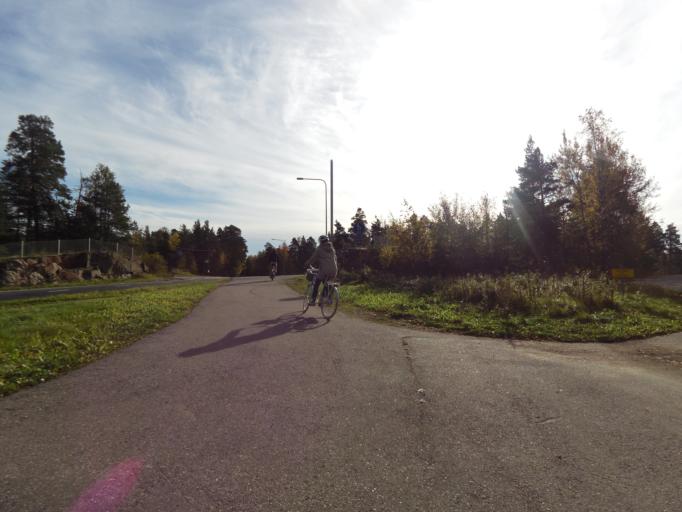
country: FI
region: Uusimaa
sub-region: Helsinki
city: Espoo
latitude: 60.1305
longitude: 24.6805
